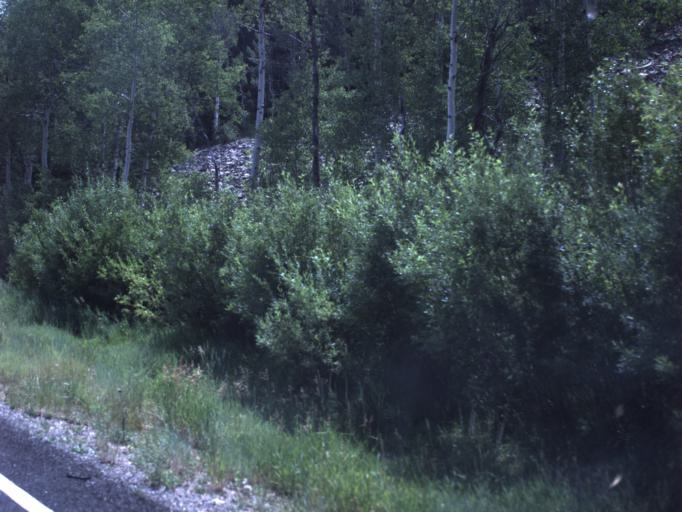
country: US
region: Utah
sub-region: Summit County
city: Francis
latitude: 40.5164
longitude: -111.0760
